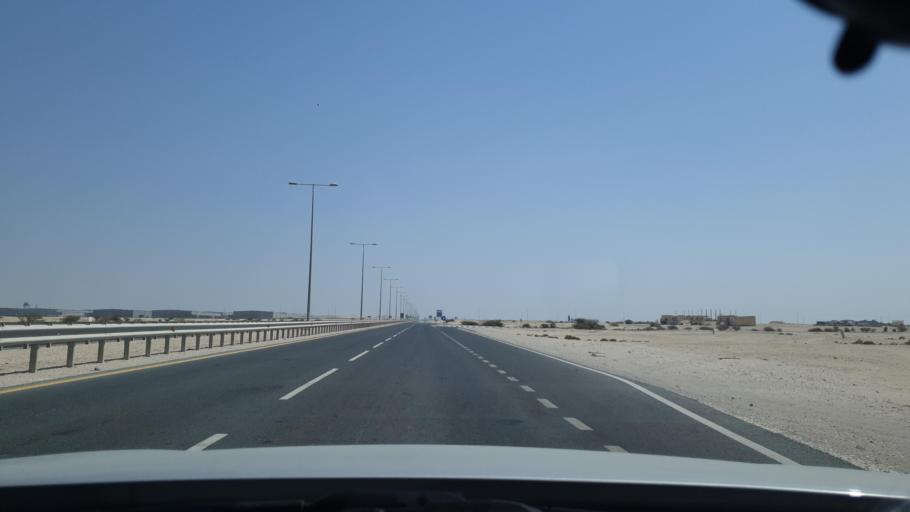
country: QA
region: Baladiyat Umm Salal
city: Umm Salal Muhammad
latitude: 25.3882
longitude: 51.3423
